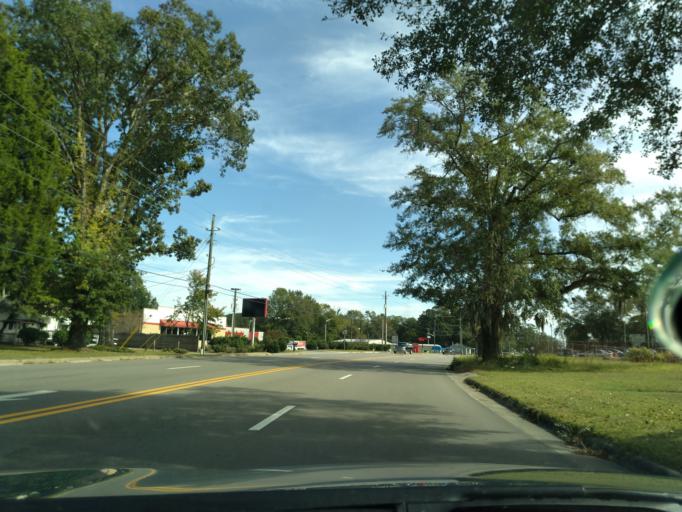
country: US
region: North Carolina
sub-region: Beaufort County
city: Washington
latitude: 35.5341
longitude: -77.0241
